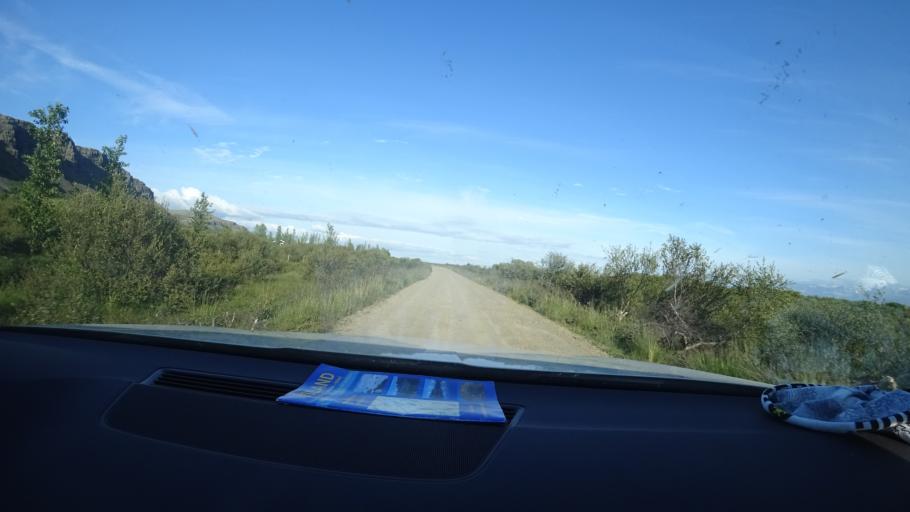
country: IS
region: West
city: Borgarnes
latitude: 64.6914
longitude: -21.9346
